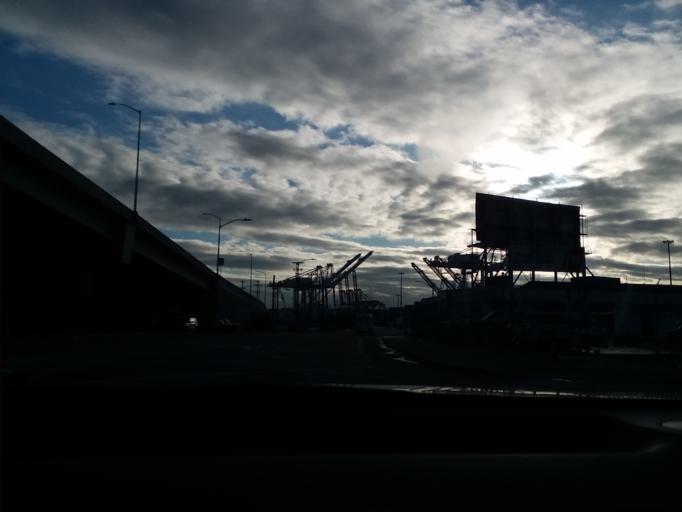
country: US
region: Washington
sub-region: King County
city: Seattle
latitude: 47.5884
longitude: -122.3386
